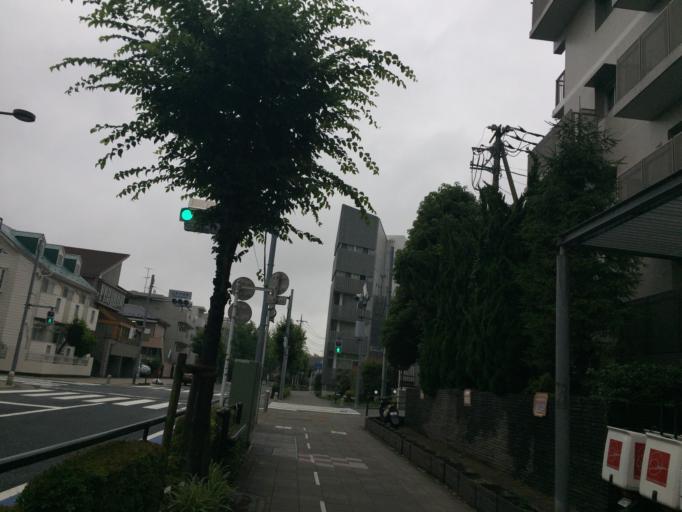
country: JP
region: Tokyo
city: Tokyo
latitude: 35.6384
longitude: 139.6739
